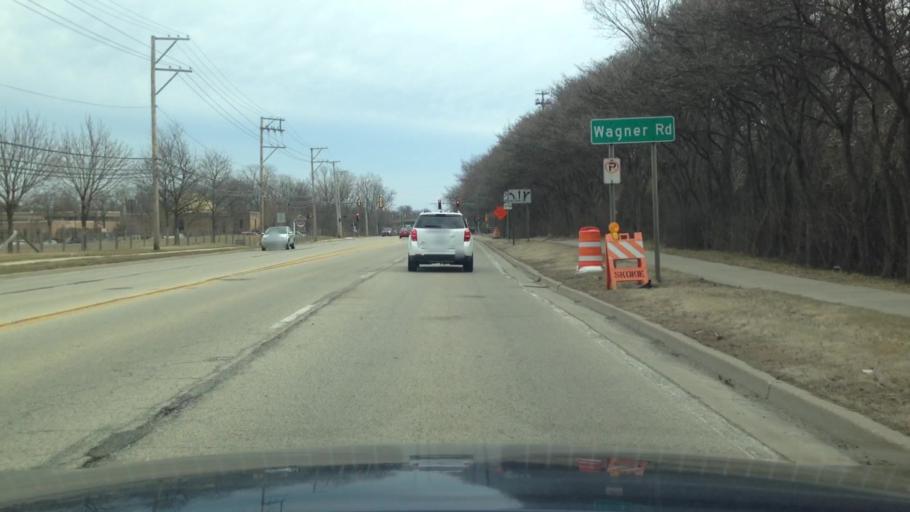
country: US
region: Illinois
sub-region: Cook County
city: Glenview
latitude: 42.0798
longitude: -87.7832
